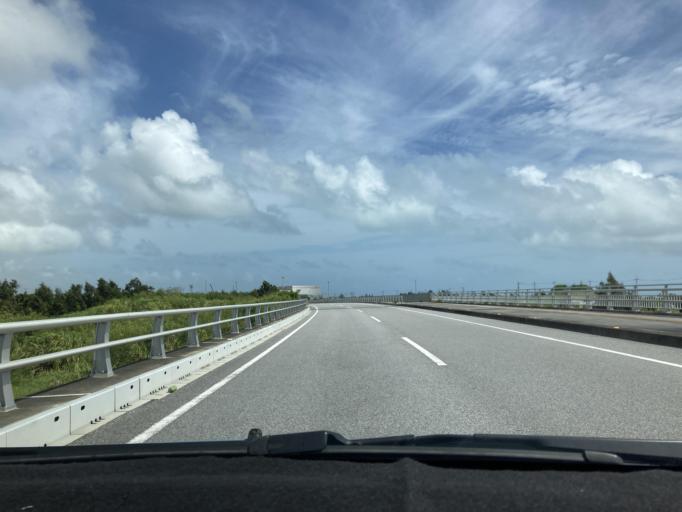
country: JP
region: Okinawa
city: Ginowan
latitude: 26.2138
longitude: 127.7700
